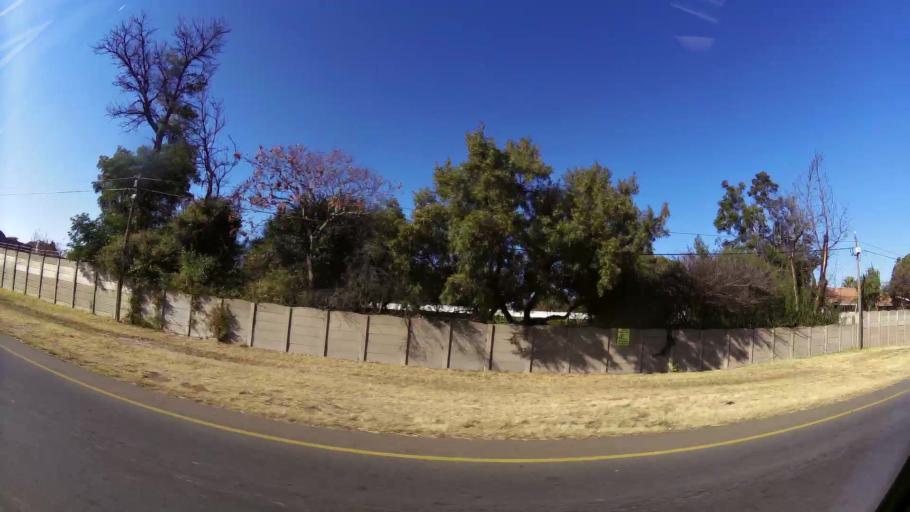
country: ZA
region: Gauteng
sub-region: Ekurhuleni Metropolitan Municipality
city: Germiston
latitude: -26.3101
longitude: 28.1003
